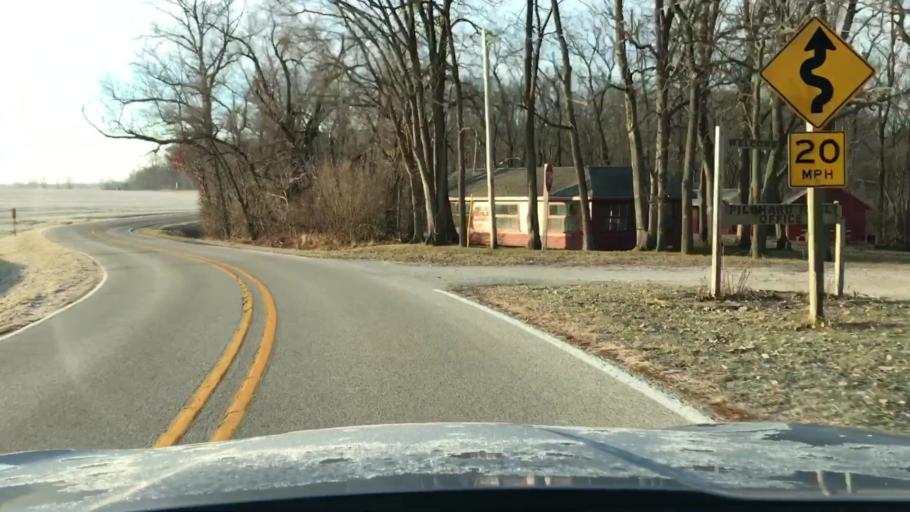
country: US
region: Illinois
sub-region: McLean County
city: Hudson
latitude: 40.6449
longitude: -88.9125
